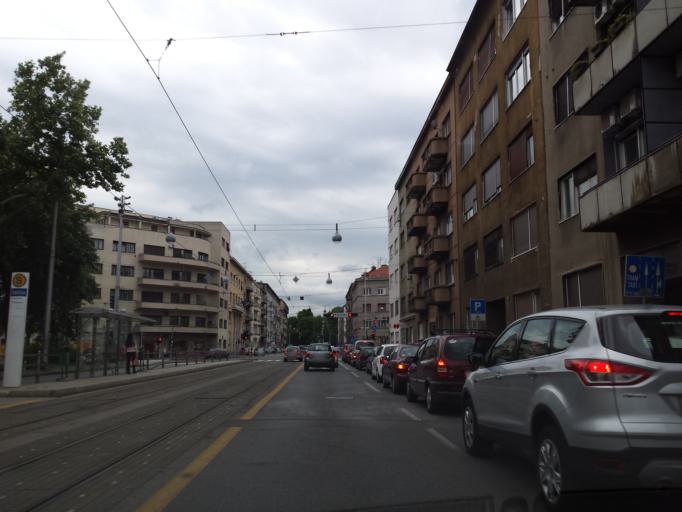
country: HR
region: Grad Zagreb
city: Zagreb
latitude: 45.8111
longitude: 15.9938
